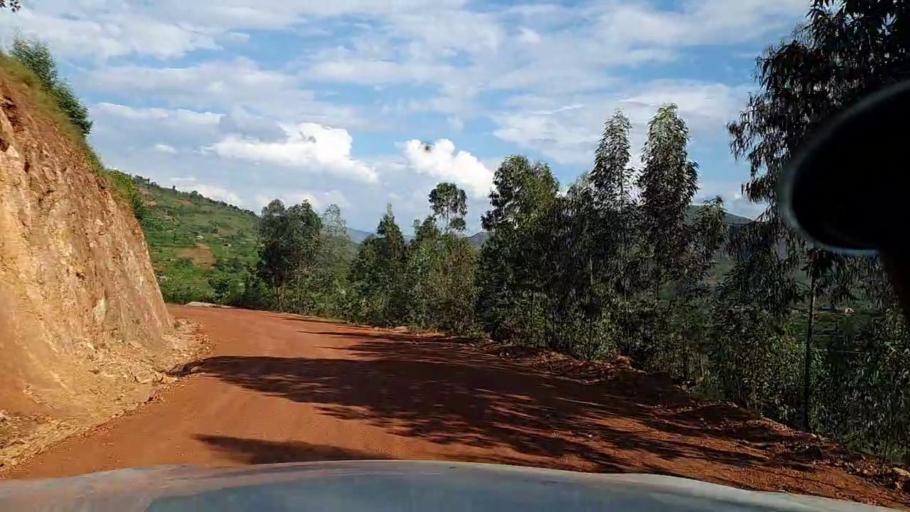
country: RW
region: Kigali
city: Kigali
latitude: -1.8480
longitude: 29.8643
